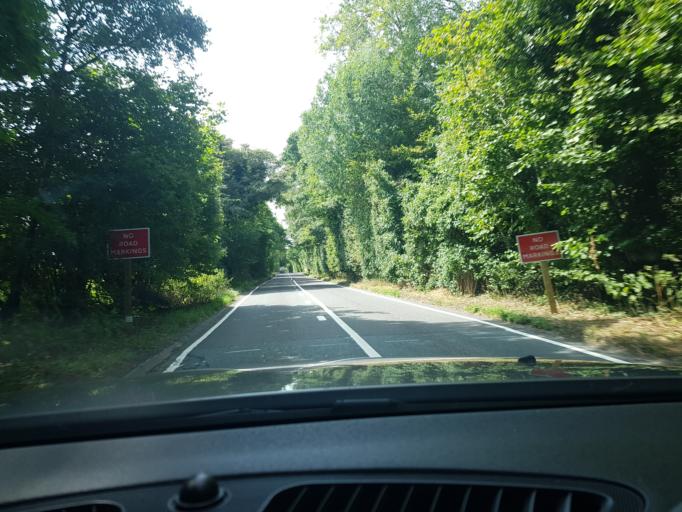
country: GB
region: England
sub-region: West Berkshire
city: Wickham
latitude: 51.4631
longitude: -1.4656
